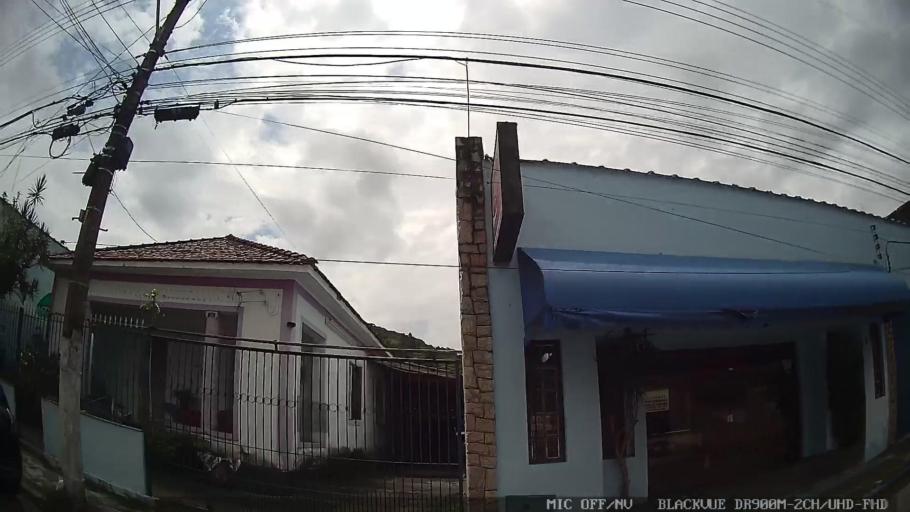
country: BR
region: Sao Paulo
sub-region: Caraguatatuba
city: Caraguatatuba
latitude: -23.6204
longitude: -45.4084
